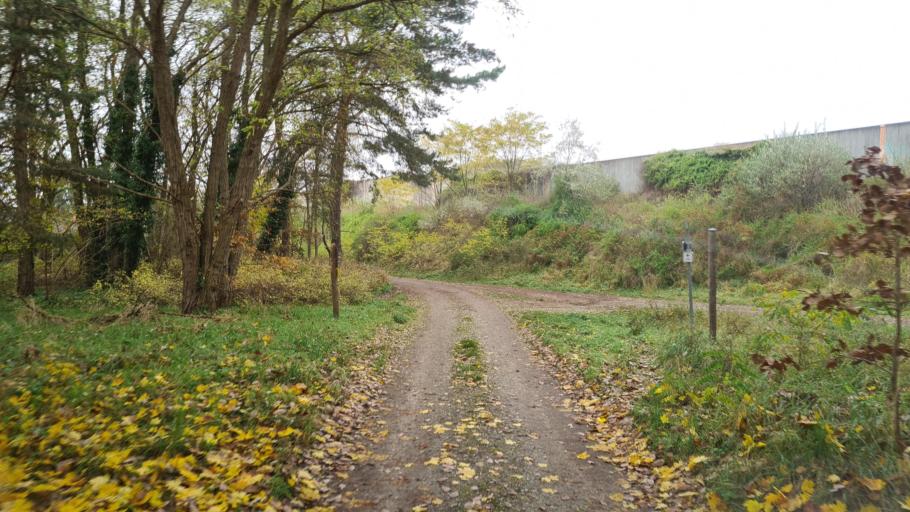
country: DE
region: Brandenburg
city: Gross Kreutz
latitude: 52.3391
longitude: 12.7354
